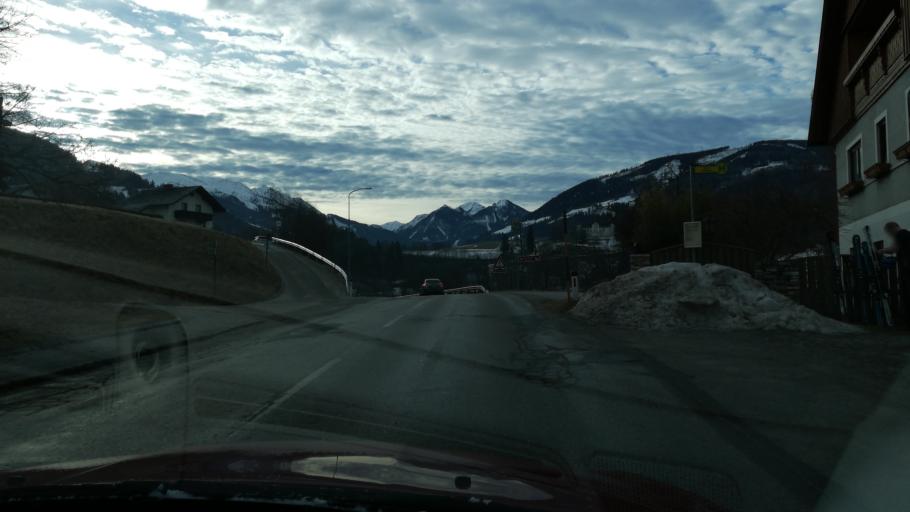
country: AT
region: Styria
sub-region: Politischer Bezirk Liezen
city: Irdning
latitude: 47.5018
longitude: 14.0964
